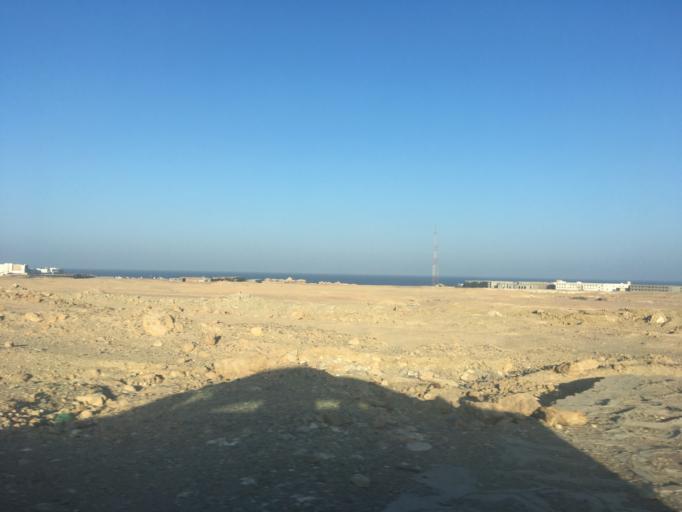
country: EG
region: Red Sea
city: Marsa Alam
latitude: 24.8710
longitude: 34.9758
